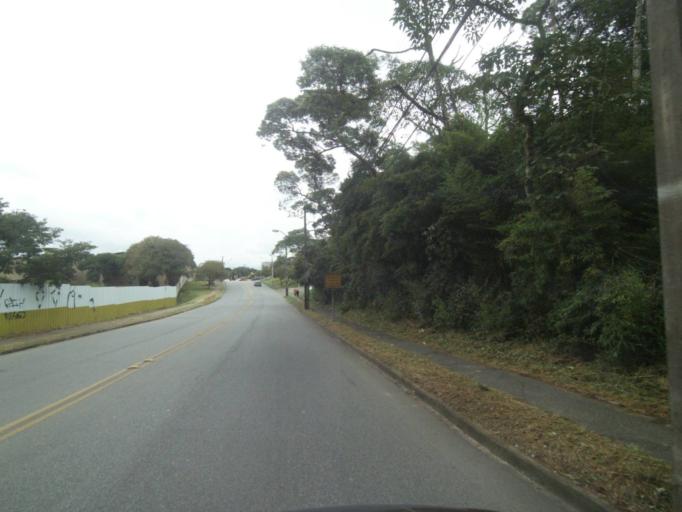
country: BR
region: Parana
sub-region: Curitiba
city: Curitiba
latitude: -25.4607
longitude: -49.3318
